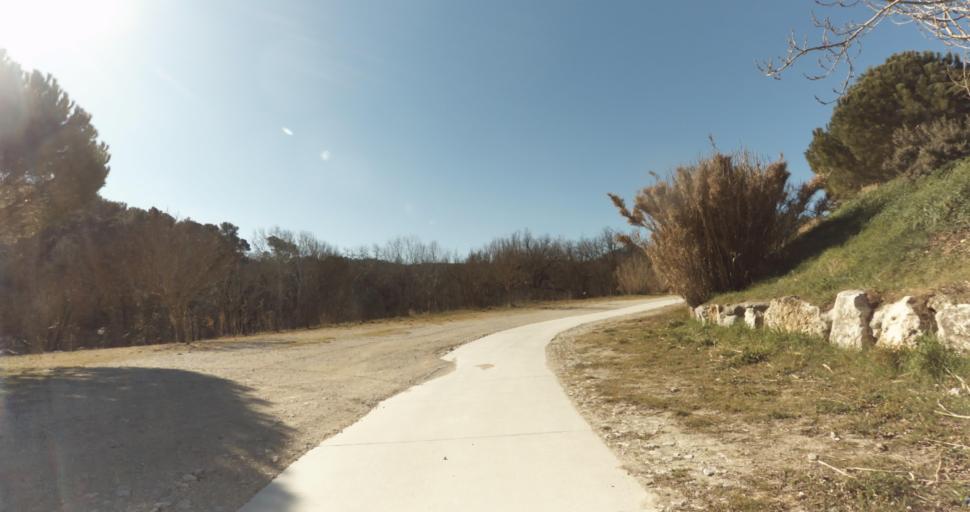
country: FR
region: Provence-Alpes-Cote d'Azur
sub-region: Departement des Bouches-du-Rhone
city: Peypin
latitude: 43.3943
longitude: 5.5641
